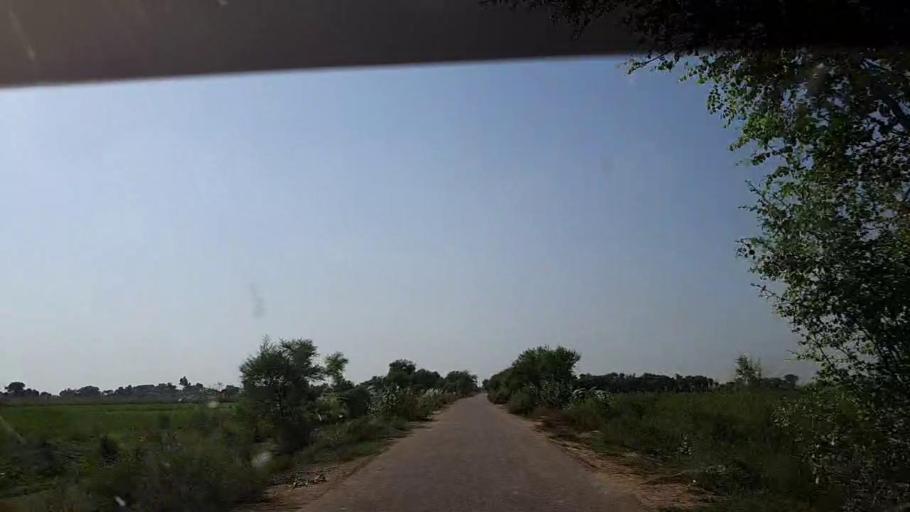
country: PK
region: Sindh
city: Tangwani
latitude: 28.2051
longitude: 69.0339
